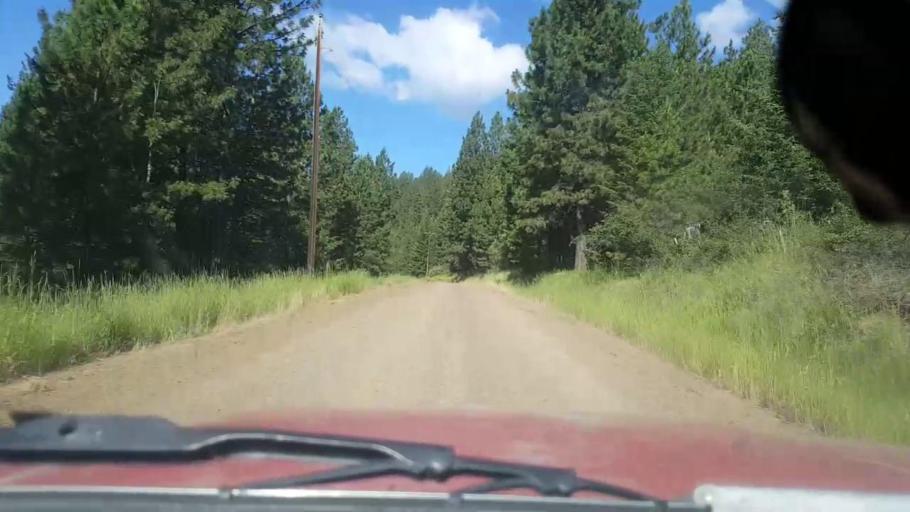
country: US
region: Washington
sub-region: Garfield County
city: Pomeroy
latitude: 46.0370
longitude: -117.4435
